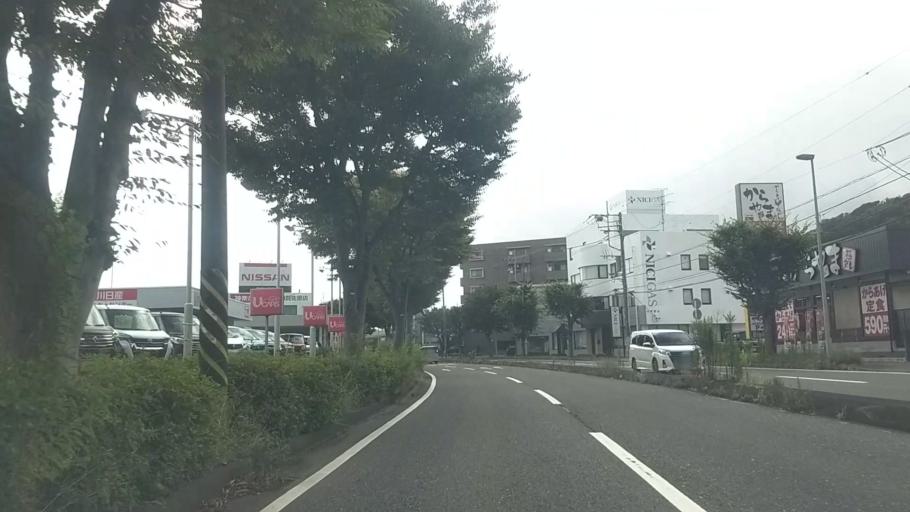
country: JP
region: Kanagawa
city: Yokosuka
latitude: 35.2440
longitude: 139.6822
